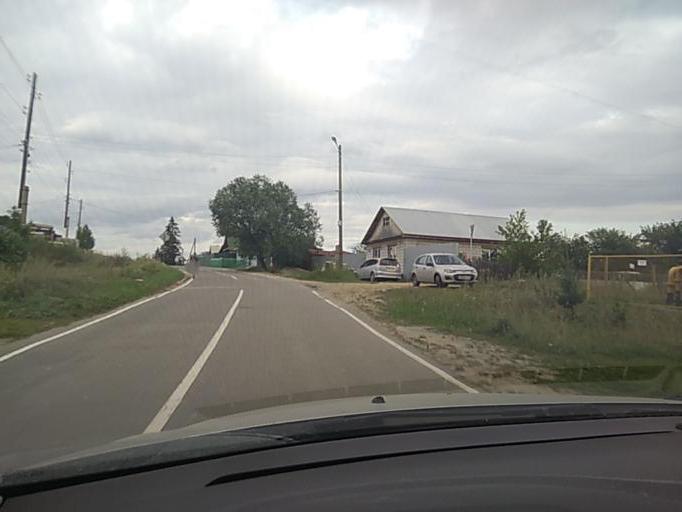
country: RU
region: Chelyabinsk
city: Kyshtym
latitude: 55.6942
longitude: 60.5439
